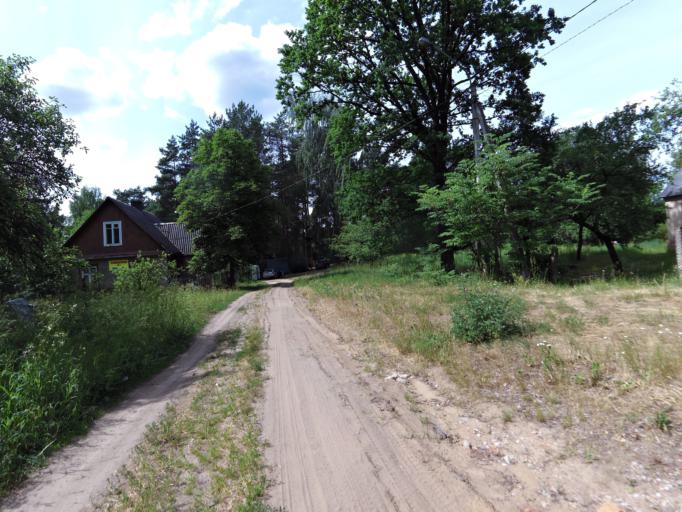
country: LT
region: Vilnius County
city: Rasos
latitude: 54.6802
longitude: 25.3555
